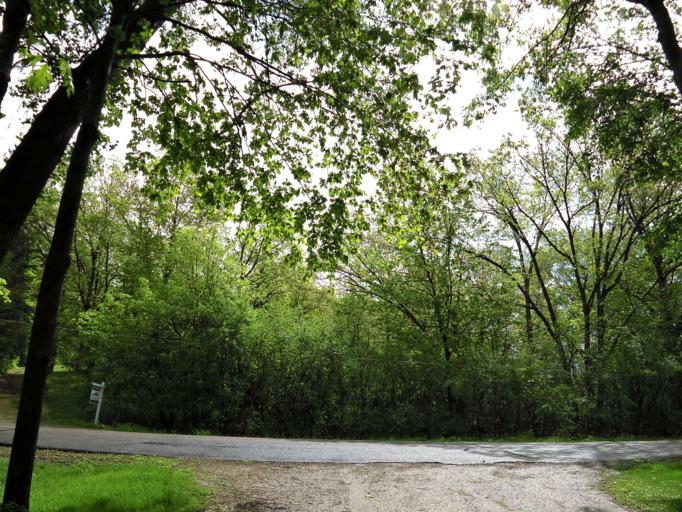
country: US
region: Minnesota
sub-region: Washington County
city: Lake Elmo
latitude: 44.9660
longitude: -92.8351
